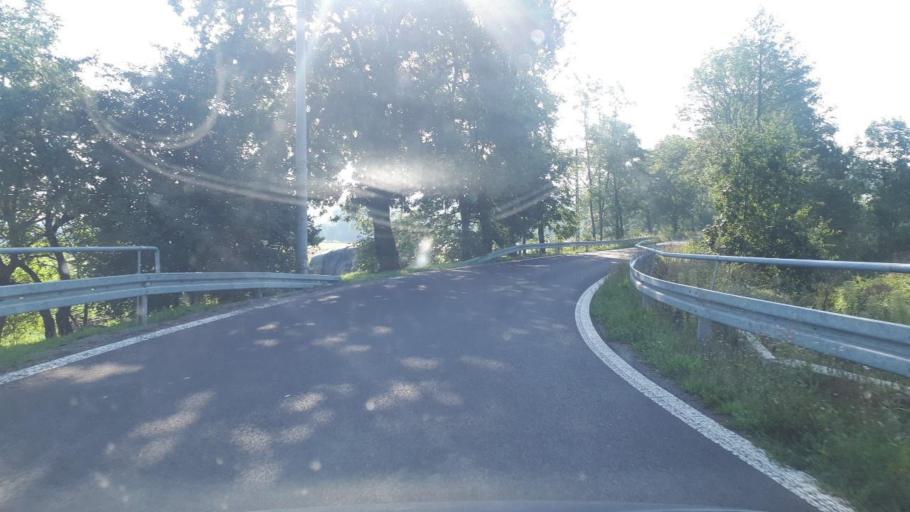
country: PL
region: Silesian Voivodeship
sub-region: Powiat cieszynski
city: Piersciec
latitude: 49.8591
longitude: 18.8441
